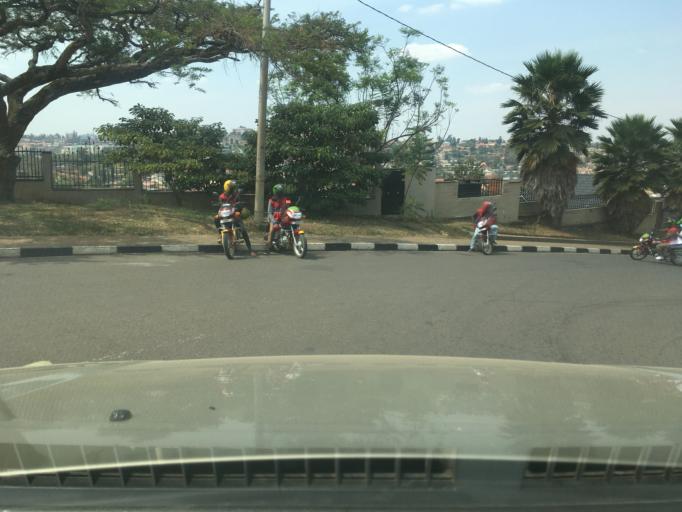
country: RW
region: Kigali
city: Kigali
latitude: -1.9535
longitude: 30.0984
